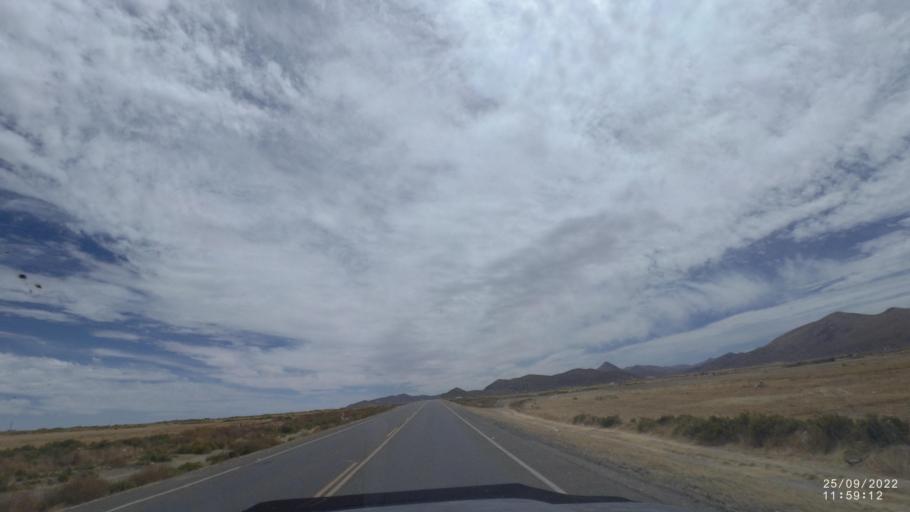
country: BO
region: Oruro
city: Challapata
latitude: -18.7915
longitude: -66.8448
